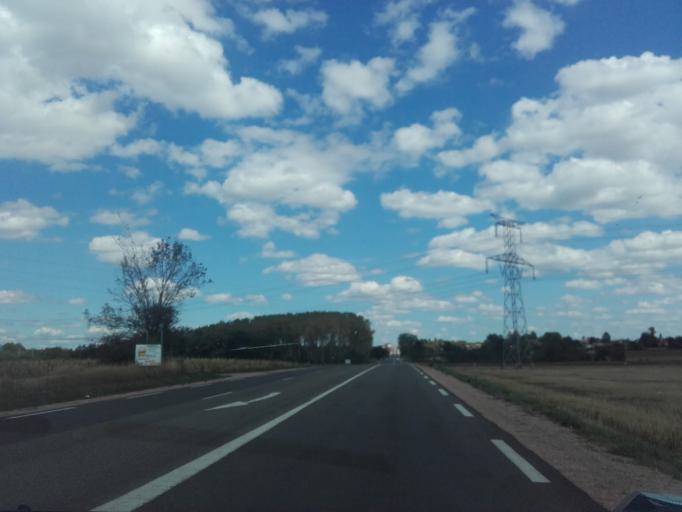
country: FR
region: Bourgogne
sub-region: Departement de Saone-et-Loire
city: La Chapelle-de-Guinchay
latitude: 46.1927
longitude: 4.7597
